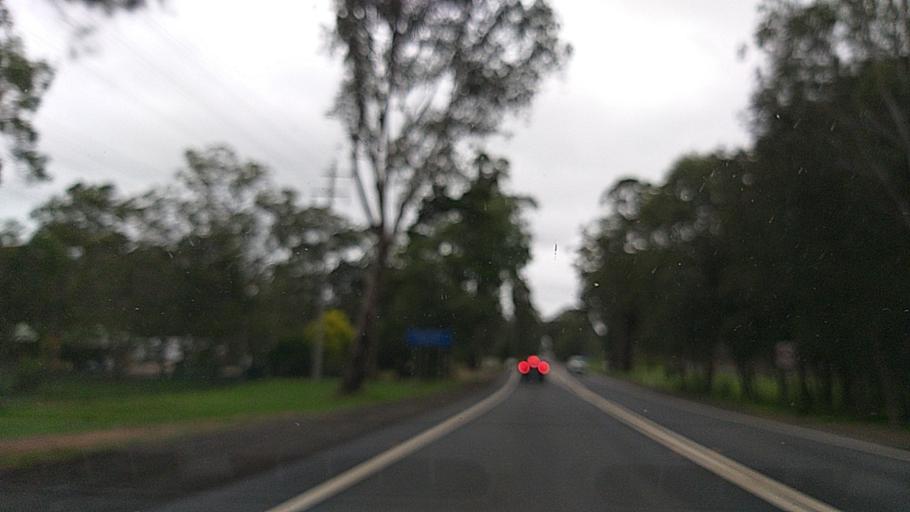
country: AU
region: New South Wales
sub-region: Hawkesbury
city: South Windsor
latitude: -33.6484
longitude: 150.7785
